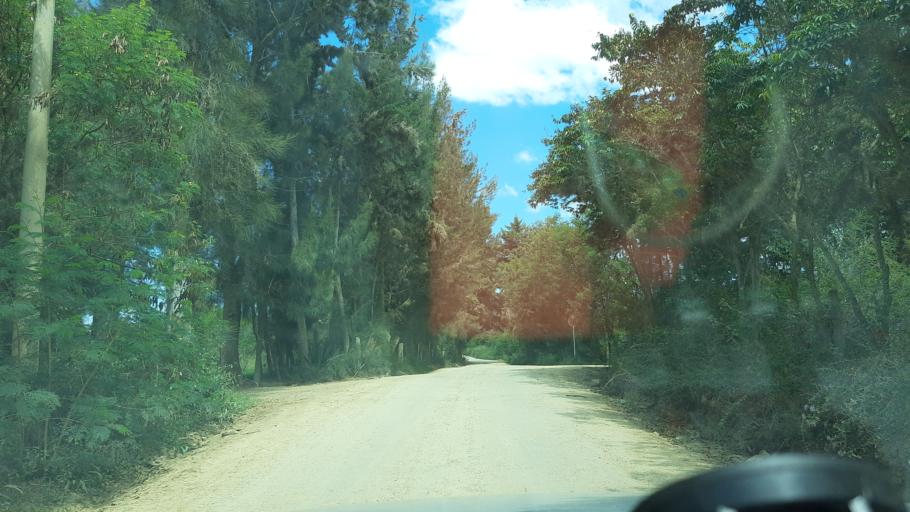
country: CO
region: Boyaca
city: Villa de Leiva
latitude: 5.6608
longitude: -73.5727
